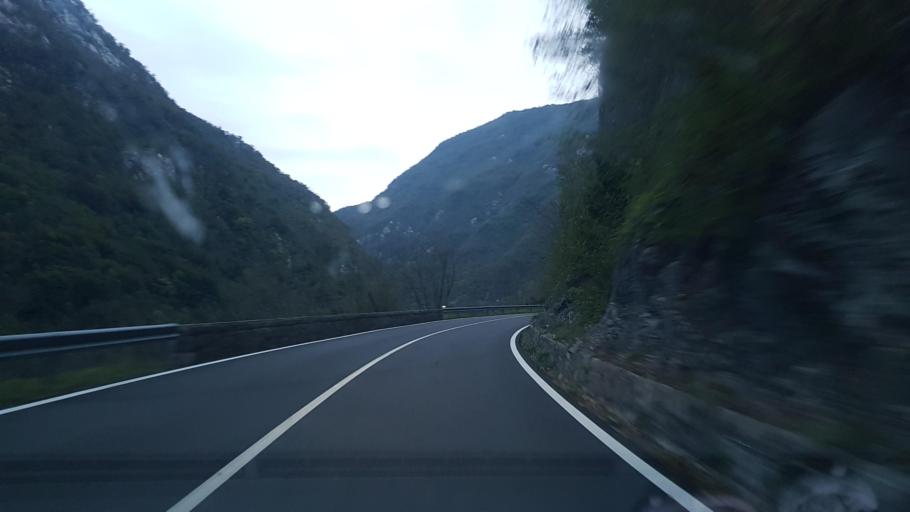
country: IT
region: Friuli Venezia Giulia
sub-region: Provincia di Pordenone
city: Anduins
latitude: 46.2534
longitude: 12.9751
